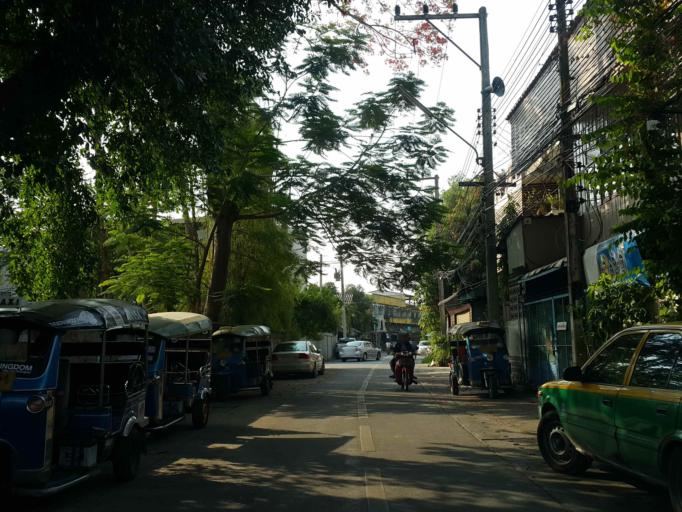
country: TH
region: Chiang Mai
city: Chiang Mai
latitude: 18.7838
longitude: 99.0077
